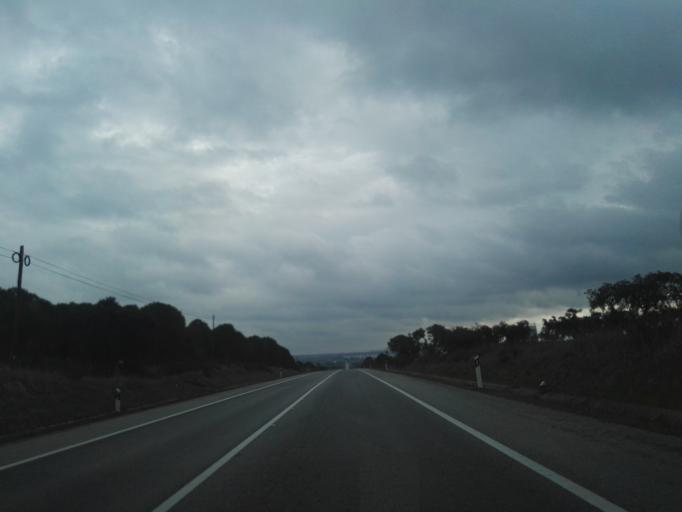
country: PT
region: Portalegre
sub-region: Arronches
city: Arronches
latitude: 39.1492
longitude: -7.3089
